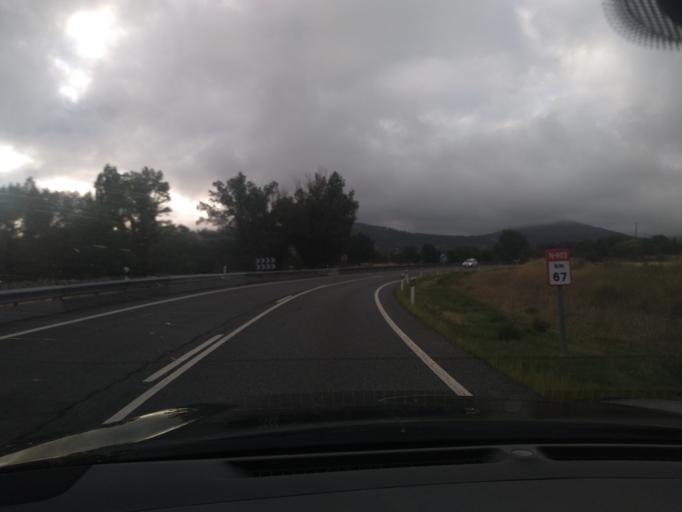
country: ES
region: Castille and Leon
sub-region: Provincia de Segovia
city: Otero de Herreros
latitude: 40.7512
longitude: -4.2002
